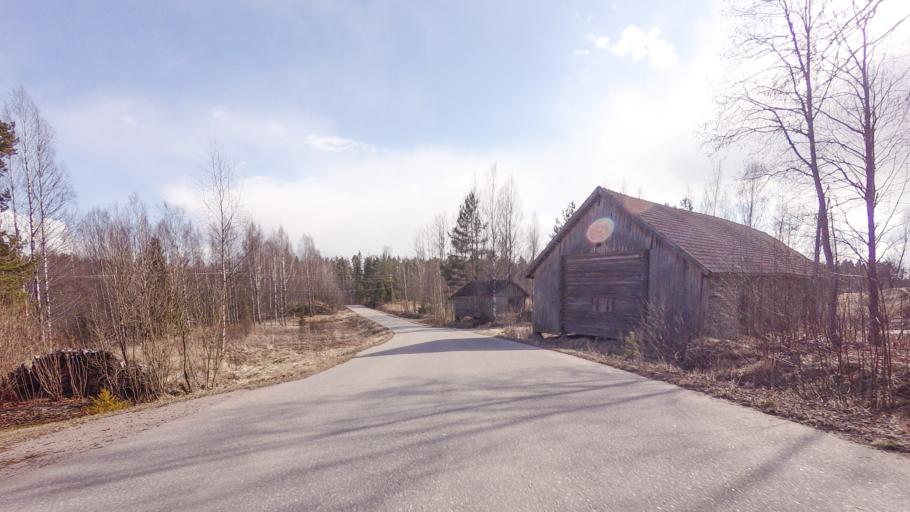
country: FI
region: Varsinais-Suomi
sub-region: Salo
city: Suomusjaervi
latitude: 60.2881
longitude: 23.6424
